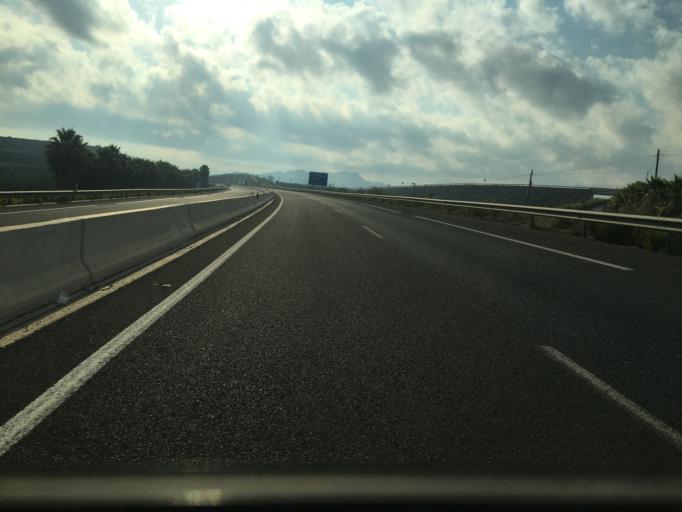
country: ES
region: Murcia
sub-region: Murcia
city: Beniel
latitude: 37.9951
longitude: -0.9982
